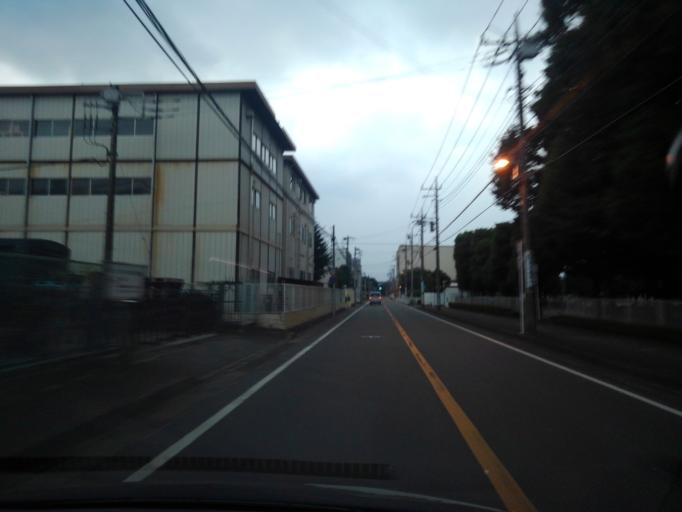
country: JP
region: Tokyo
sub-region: Machida-shi
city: Machida
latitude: 35.5777
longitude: 139.3919
